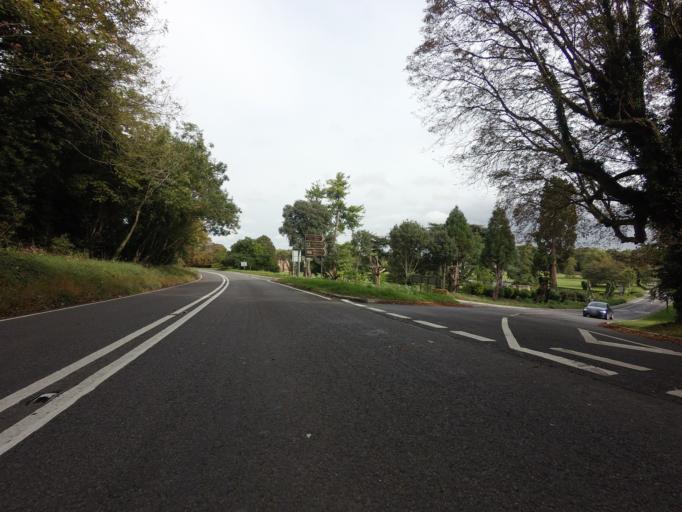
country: GB
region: England
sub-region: Essex
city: Saffron Walden
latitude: 52.0201
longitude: 0.2144
